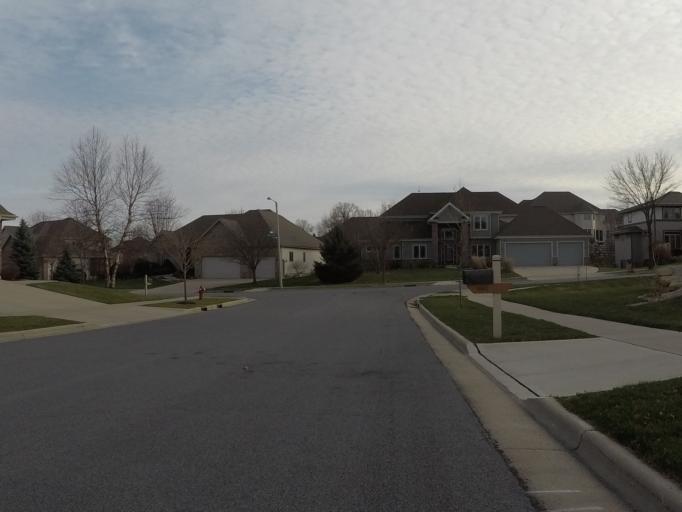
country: US
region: Wisconsin
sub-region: Dane County
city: Middleton
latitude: 43.0797
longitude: -89.5582
